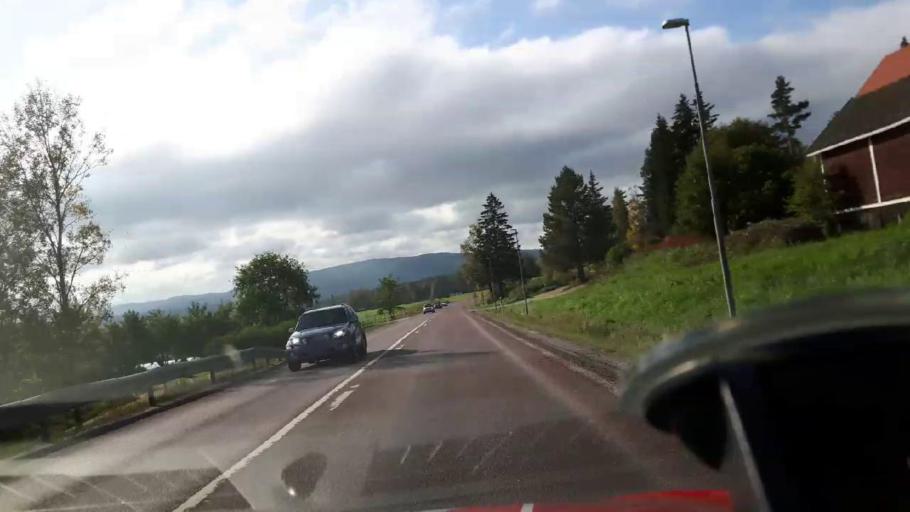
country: SE
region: Gaevleborg
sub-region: Ljusdals Kommun
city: Jaervsoe
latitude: 61.6994
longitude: 16.1629
